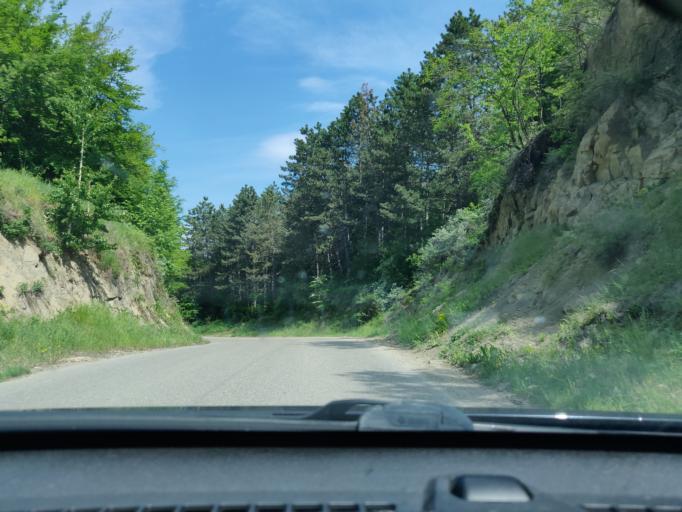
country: RO
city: Vizantea-Manastireasca
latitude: 45.9624
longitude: 26.8213
